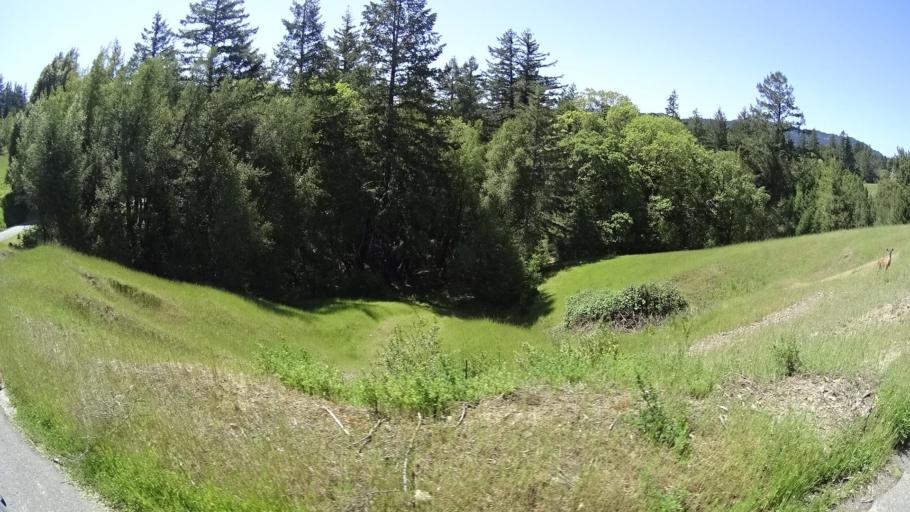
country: US
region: California
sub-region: Humboldt County
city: Redway
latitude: 40.1421
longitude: -124.0010
